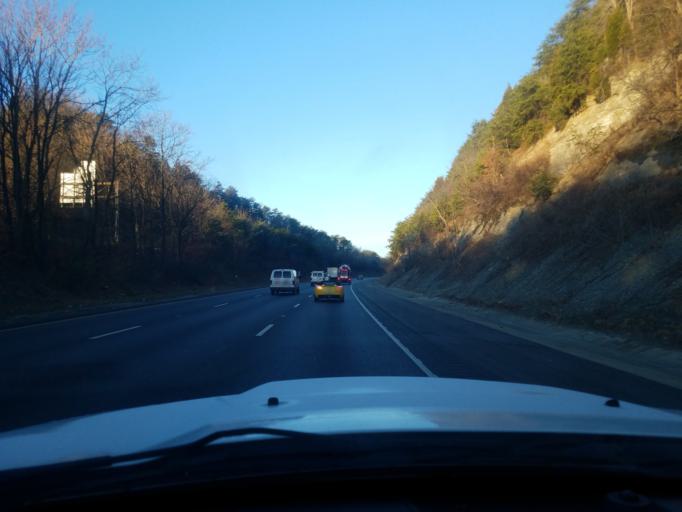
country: US
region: Indiana
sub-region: Floyd County
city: New Albany
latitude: 38.3015
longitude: -85.8669
